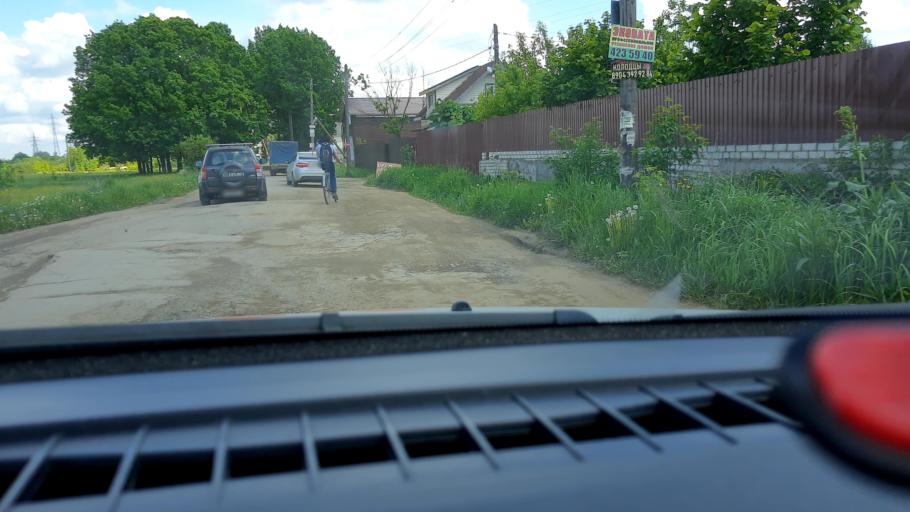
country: RU
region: Nizjnij Novgorod
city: Gorbatovka
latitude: 56.3877
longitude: 43.8087
